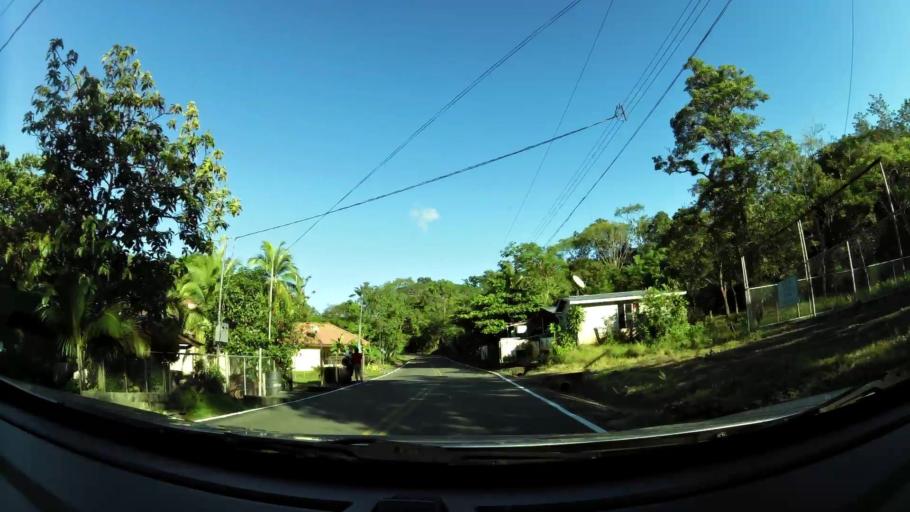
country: CR
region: Guanacaste
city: Juntas
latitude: 10.2032
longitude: -84.8458
